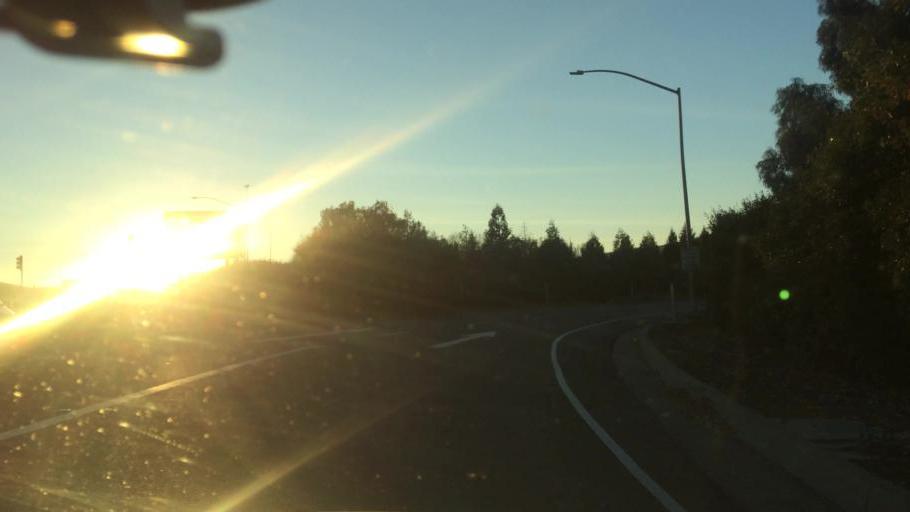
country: US
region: California
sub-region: Contra Costa County
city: San Ramon
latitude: 37.7784
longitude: -121.9732
